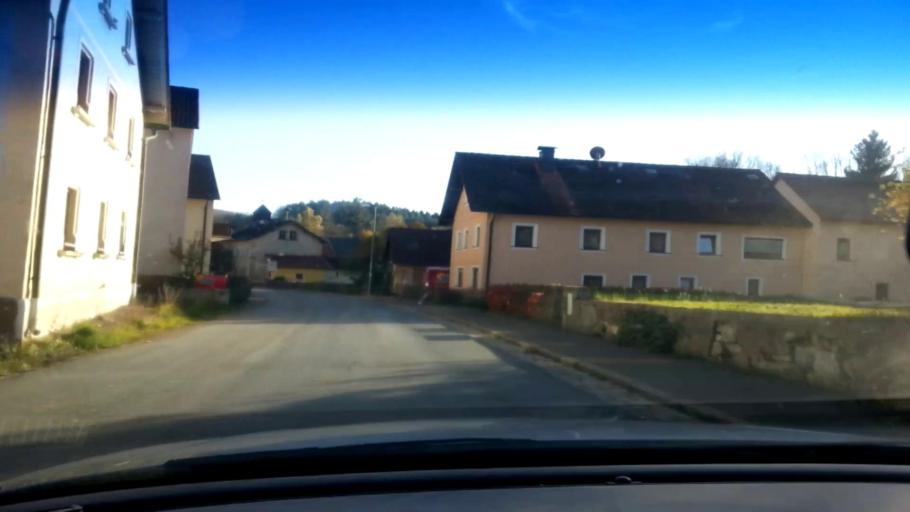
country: DE
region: Bavaria
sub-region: Upper Franconia
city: Heiligenstadt
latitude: 49.8843
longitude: 11.1282
